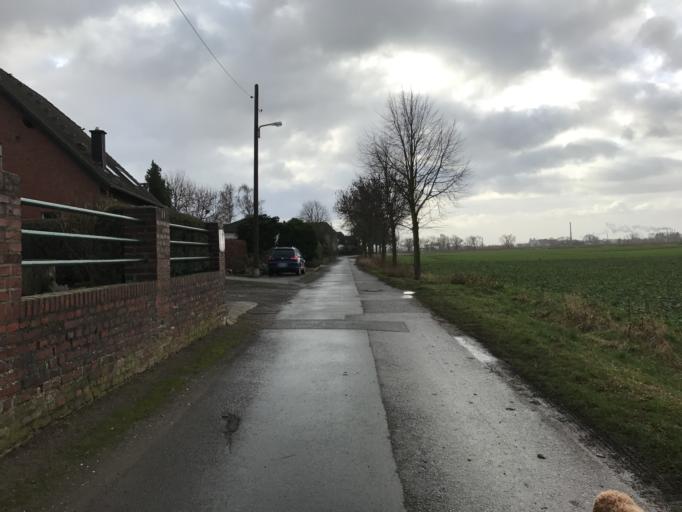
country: DE
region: North Rhine-Westphalia
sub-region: Regierungsbezirk Dusseldorf
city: Meerbusch
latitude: 51.3568
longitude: 6.6810
